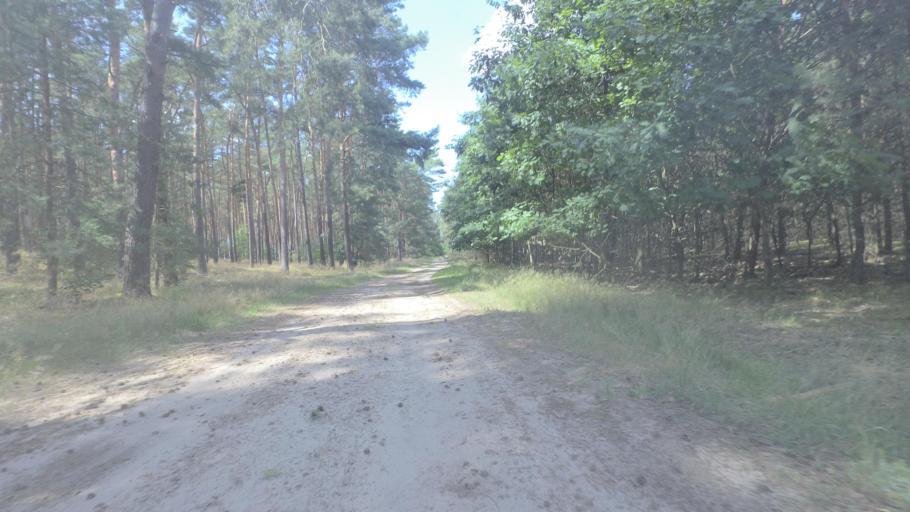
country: DE
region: Brandenburg
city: Am Mellensee
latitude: 52.2300
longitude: 13.3911
